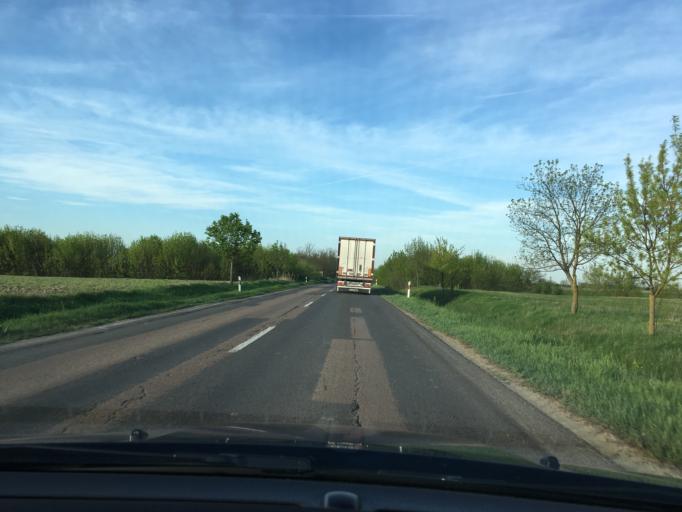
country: HU
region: Hajdu-Bihar
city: Berettyoujfalu
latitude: 47.1713
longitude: 21.5175
